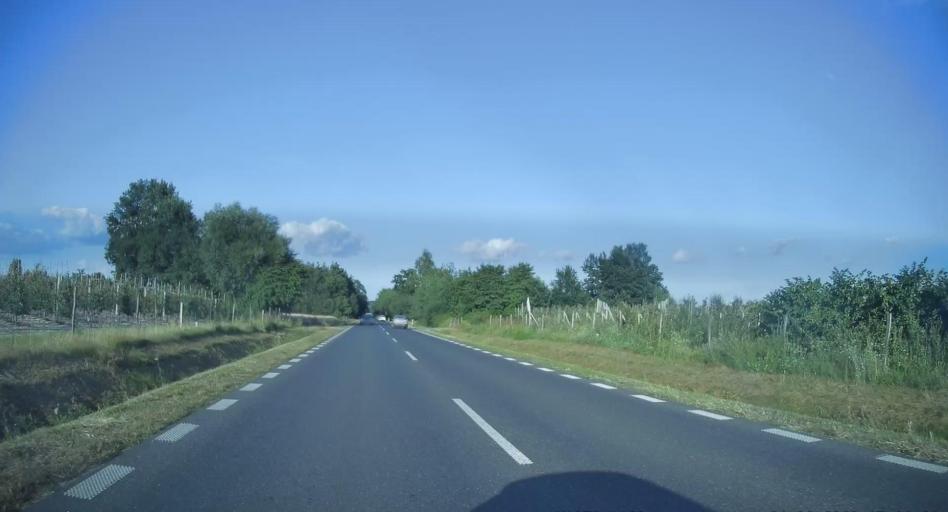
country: PL
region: Lodz Voivodeship
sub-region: Powiat rawski
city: Regnow
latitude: 51.7915
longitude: 20.3726
